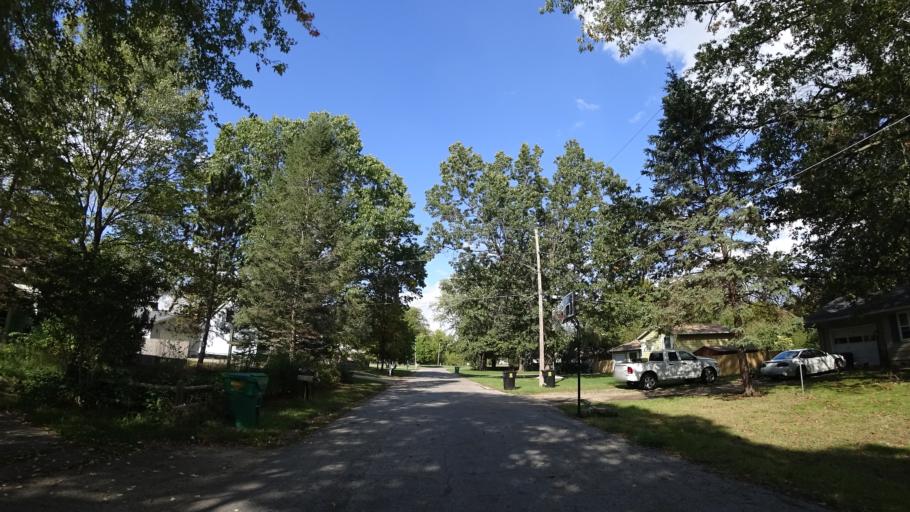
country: US
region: Michigan
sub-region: Saint Joseph County
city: Three Rivers
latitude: 41.9526
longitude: -85.6146
